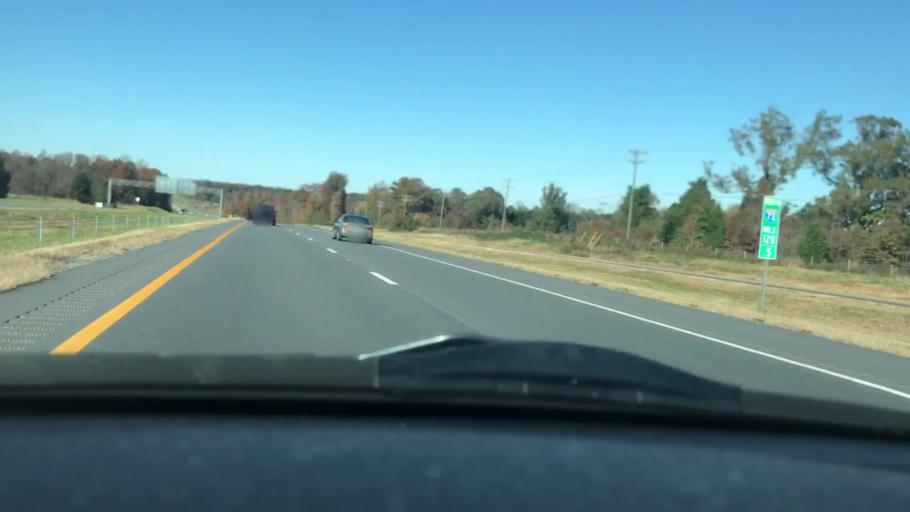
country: US
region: North Carolina
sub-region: Guilford County
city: Summerfield
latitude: 36.2488
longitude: -79.9211
